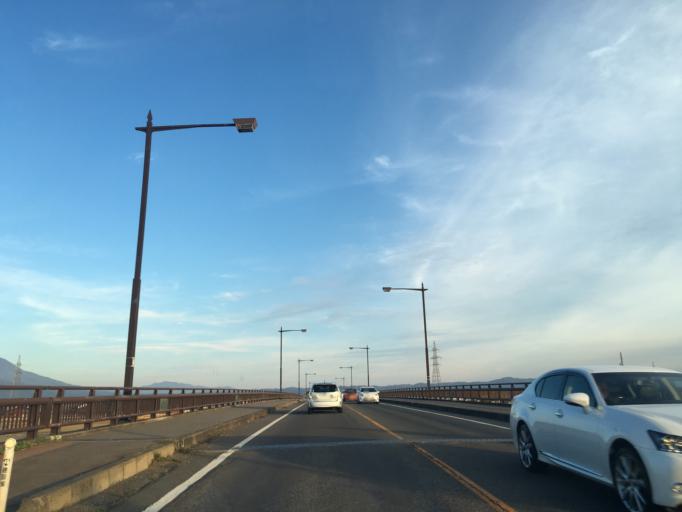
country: JP
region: Fukushima
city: Kitakata
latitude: 37.5570
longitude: 139.8577
